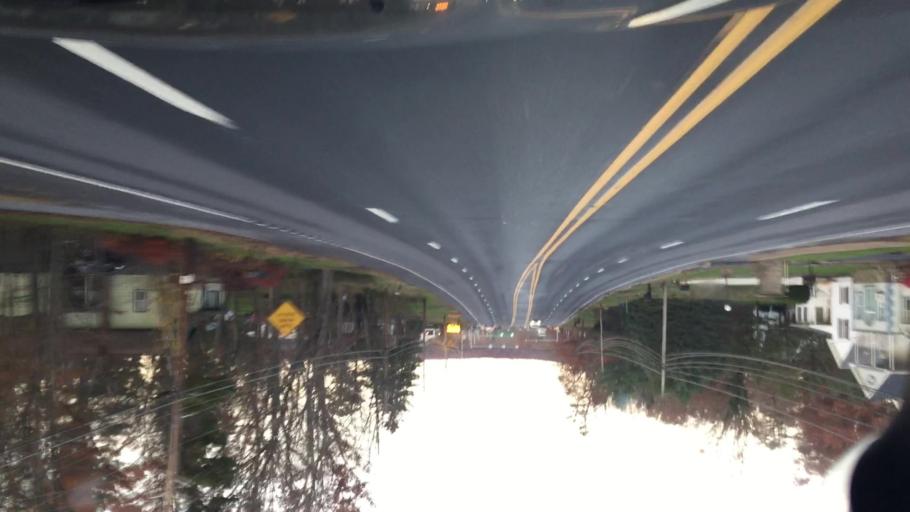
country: US
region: Pennsylvania
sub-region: Luzerne County
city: Oakdale
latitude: 41.0477
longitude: -75.9572
